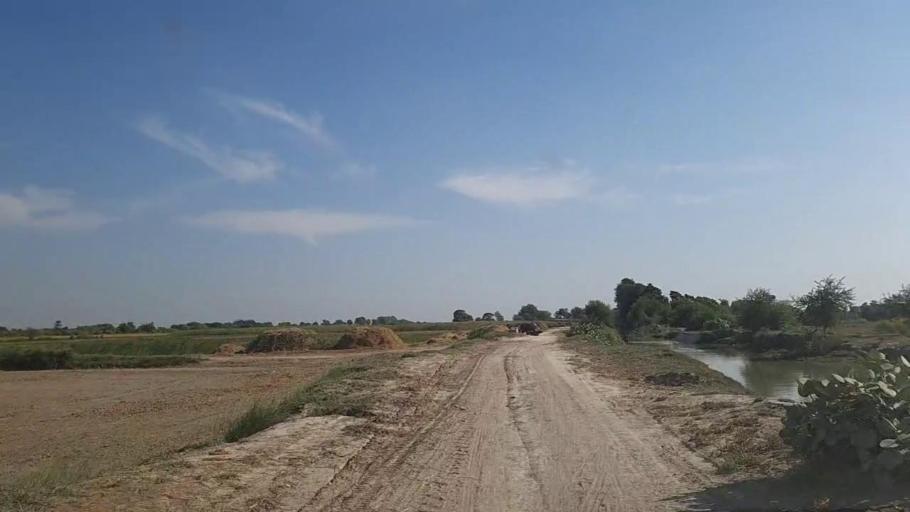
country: PK
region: Sindh
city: Bulri
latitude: 24.8607
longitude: 68.2869
